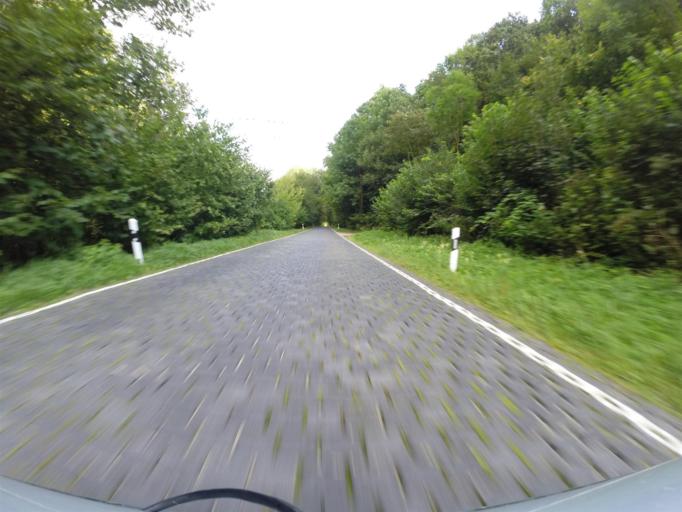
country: DE
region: Thuringia
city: Lehesten
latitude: 50.9572
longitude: 11.5930
